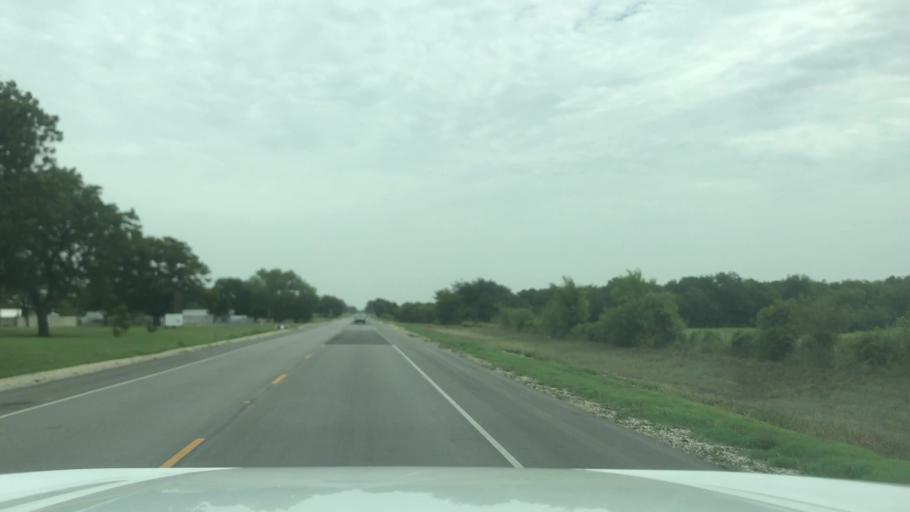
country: US
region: Texas
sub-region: Erath County
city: Dublin
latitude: 32.0891
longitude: -98.2922
